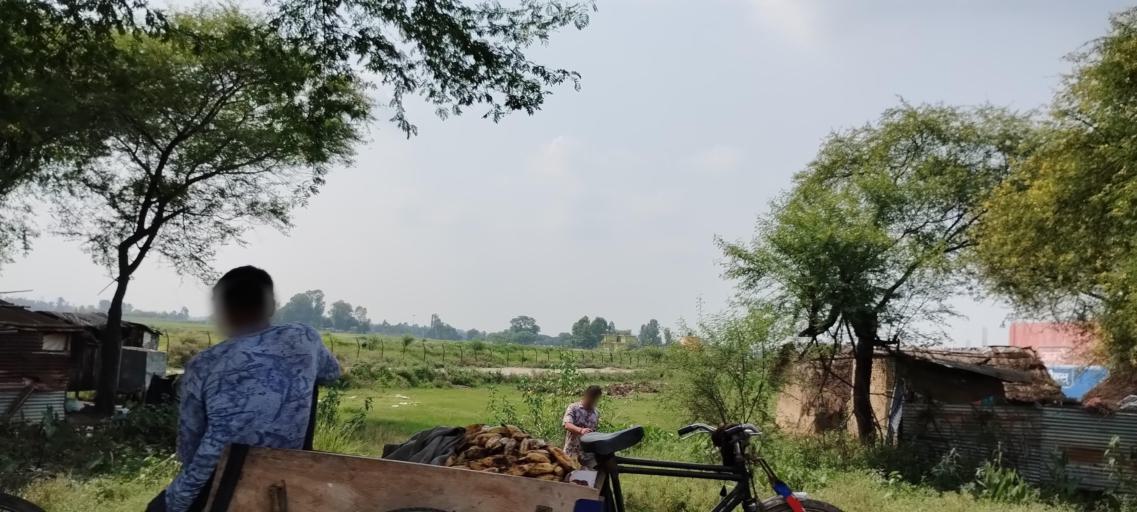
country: NP
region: Mid Western
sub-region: Bheri Zone
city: Nepalgunj
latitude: 28.1021
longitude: 81.6542
